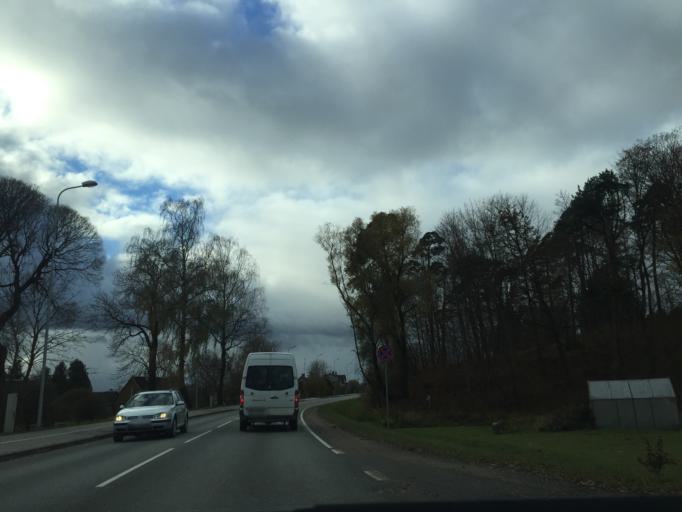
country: LV
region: Tukuma Rajons
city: Tukums
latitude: 56.9610
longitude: 23.1338
